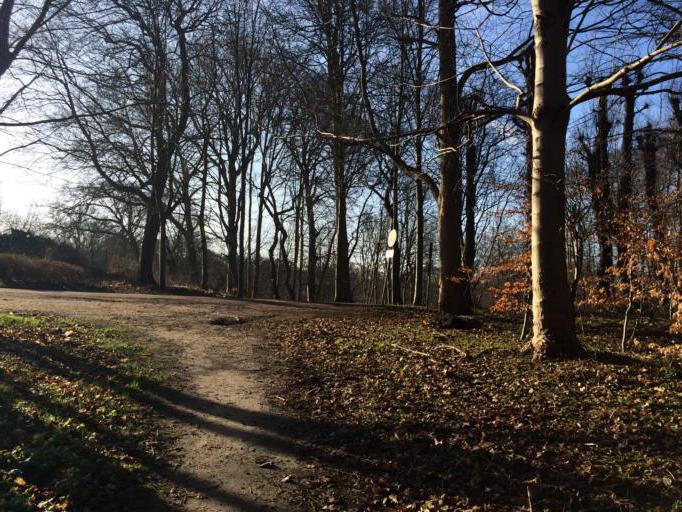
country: DK
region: Capital Region
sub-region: Fureso Kommune
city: Farum
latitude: 55.8097
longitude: 12.3704
